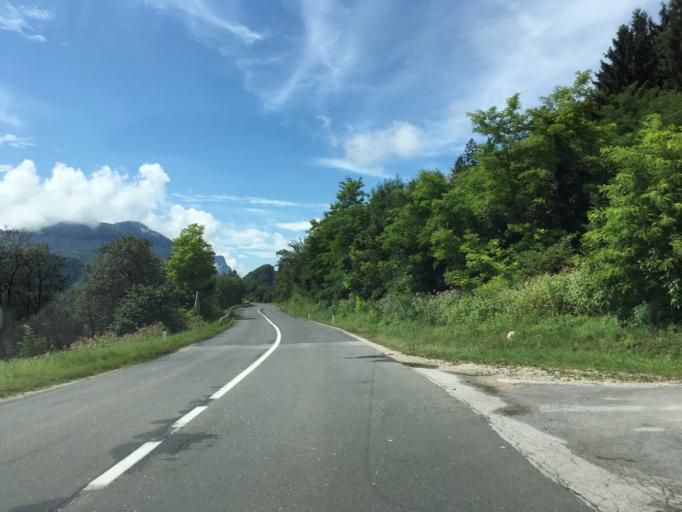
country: SI
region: Zirovnica
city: Zirovnica
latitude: 46.4141
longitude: 14.1254
